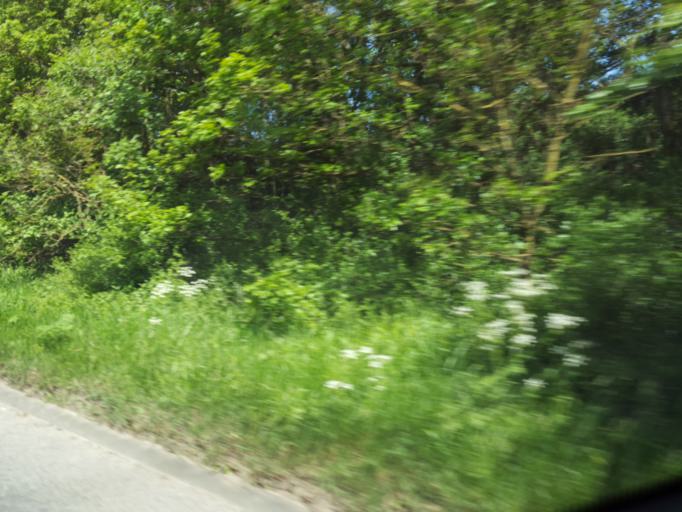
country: GB
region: England
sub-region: Wiltshire
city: Malmesbury
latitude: 51.5861
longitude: -2.0888
